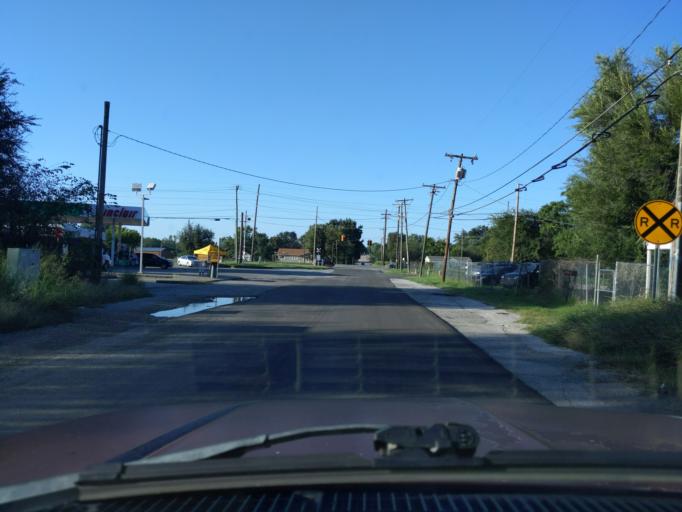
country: US
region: Oklahoma
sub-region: Tulsa County
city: Sand Springs
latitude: 36.1467
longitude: -96.0652
